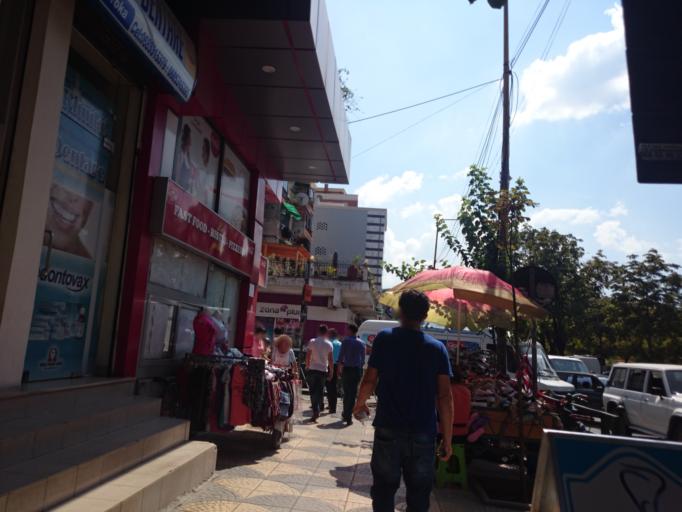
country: AL
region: Tirane
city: Tirana
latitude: 41.3247
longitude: 19.8253
